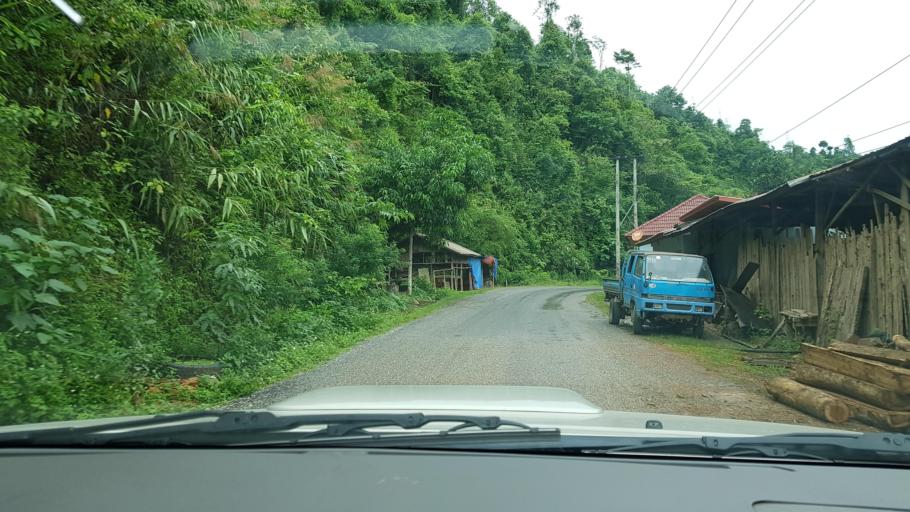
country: LA
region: Oudomxai
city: Muang La
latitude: 21.0882
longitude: 102.2422
